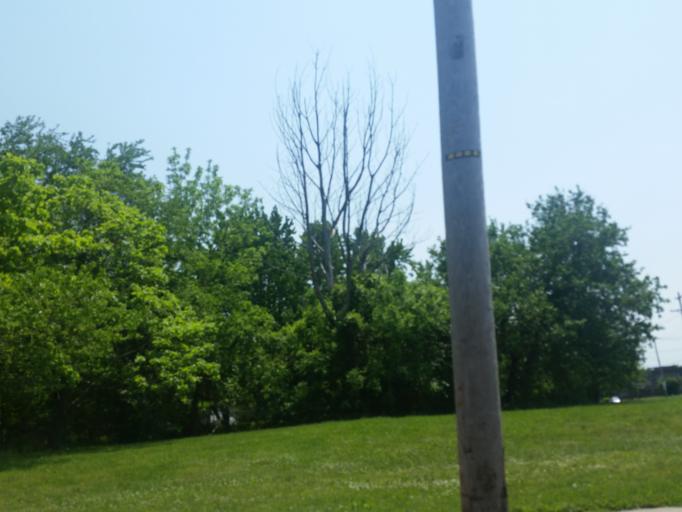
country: US
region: Ohio
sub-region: Cuyahoga County
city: Bratenahl
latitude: 41.4934
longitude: -81.6329
